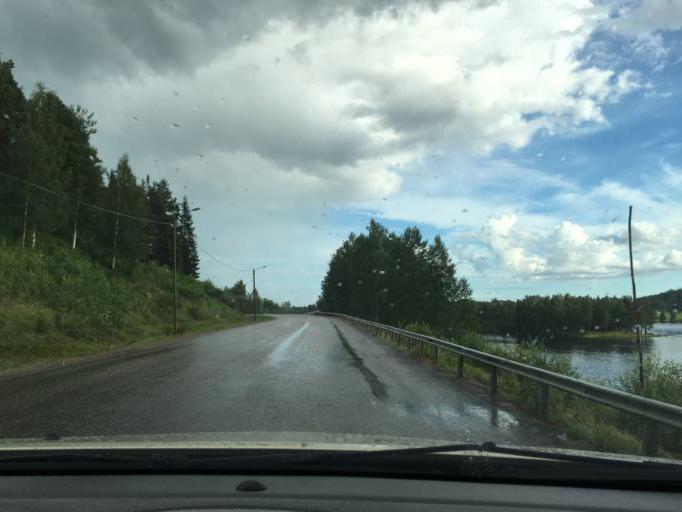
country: SE
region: Norrbotten
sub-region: Kalix Kommun
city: Rolfs
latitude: 65.9295
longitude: 22.8967
